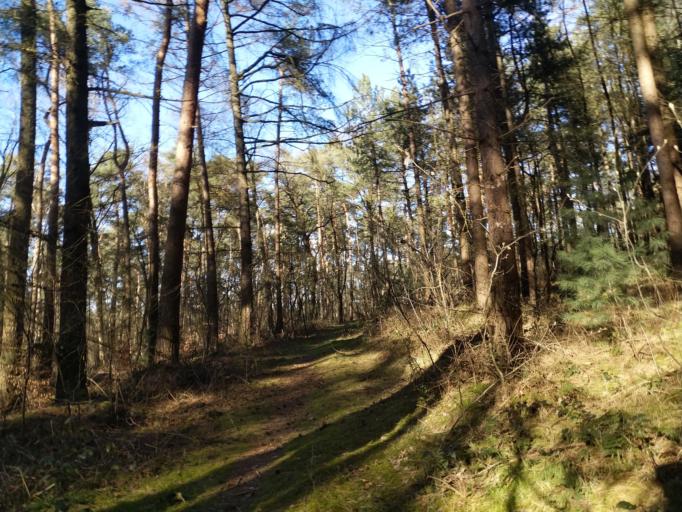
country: DE
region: North Rhine-Westphalia
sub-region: Regierungsbezirk Munster
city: Haltern
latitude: 51.7241
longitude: 7.2053
